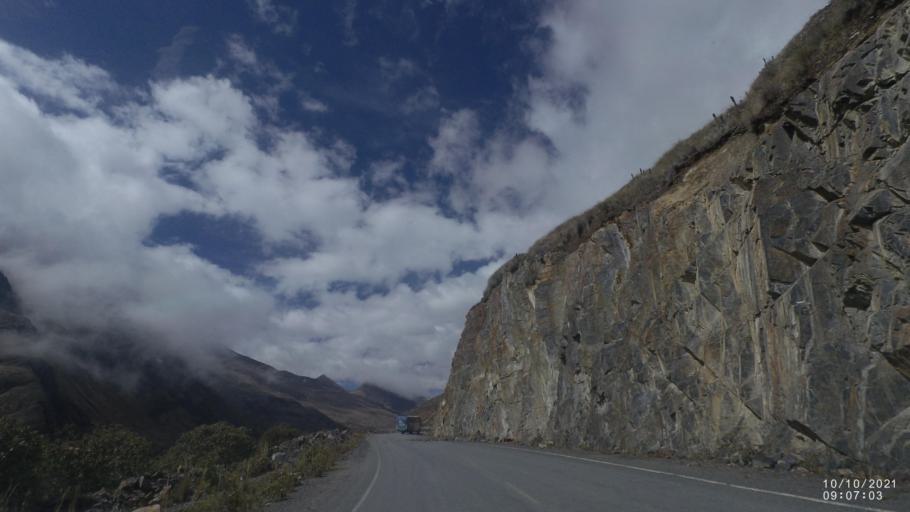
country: BO
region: La Paz
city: Quime
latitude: -17.0076
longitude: -67.2741
